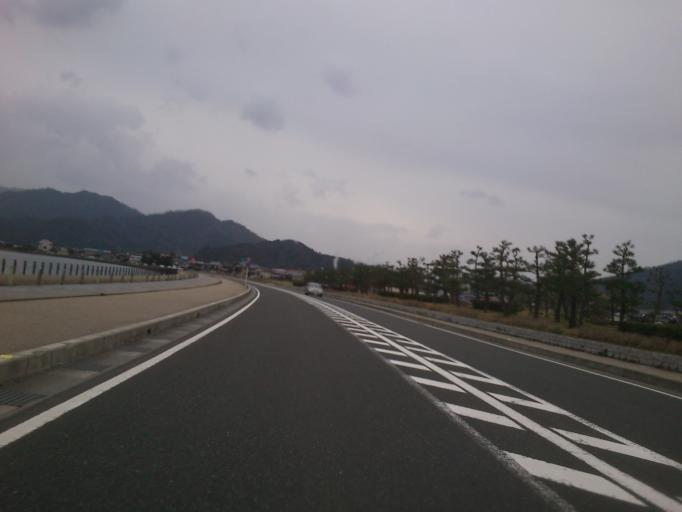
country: JP
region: Kyoto
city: Miyazu
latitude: 35.5678
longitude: 135.1569
